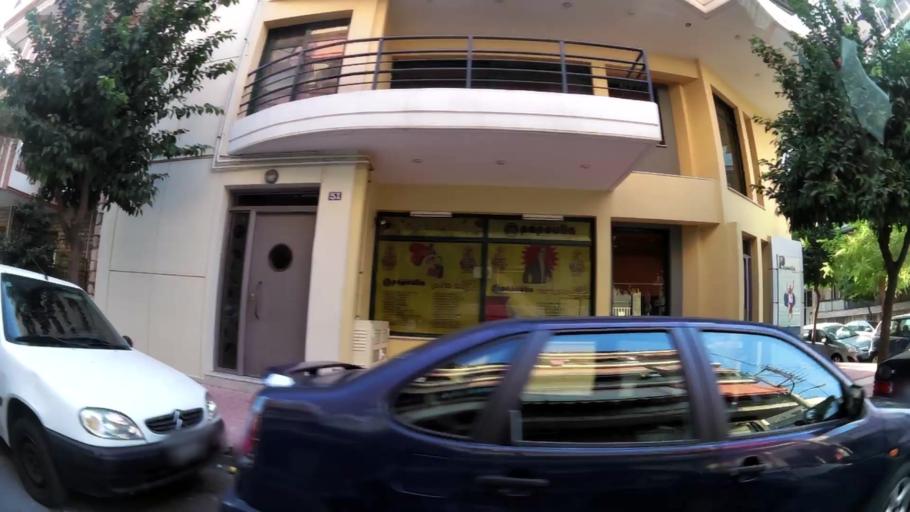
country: GR
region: Attica
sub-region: Nomarchia Athinas
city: Kallithea
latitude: 37.9562
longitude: 23.7088
